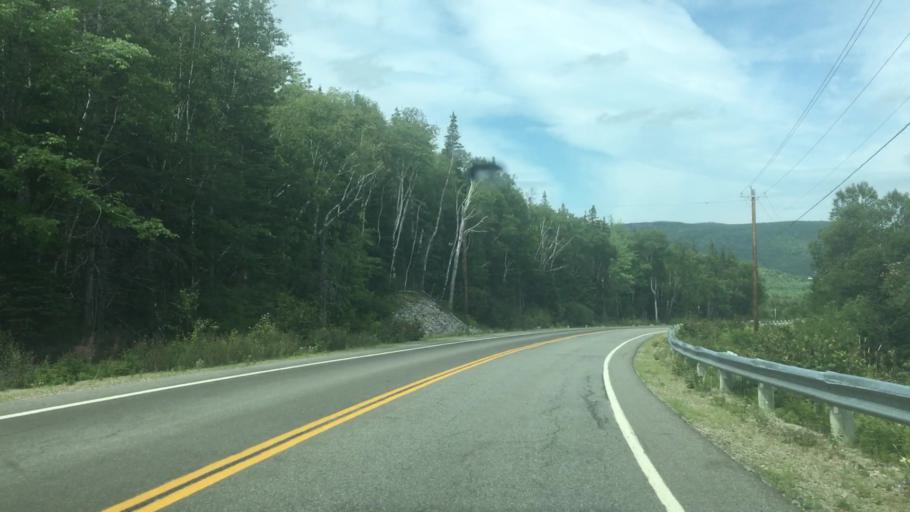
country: CA
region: Nova Scotia
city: Sydney Mines
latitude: 46.5388
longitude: -60.4140
